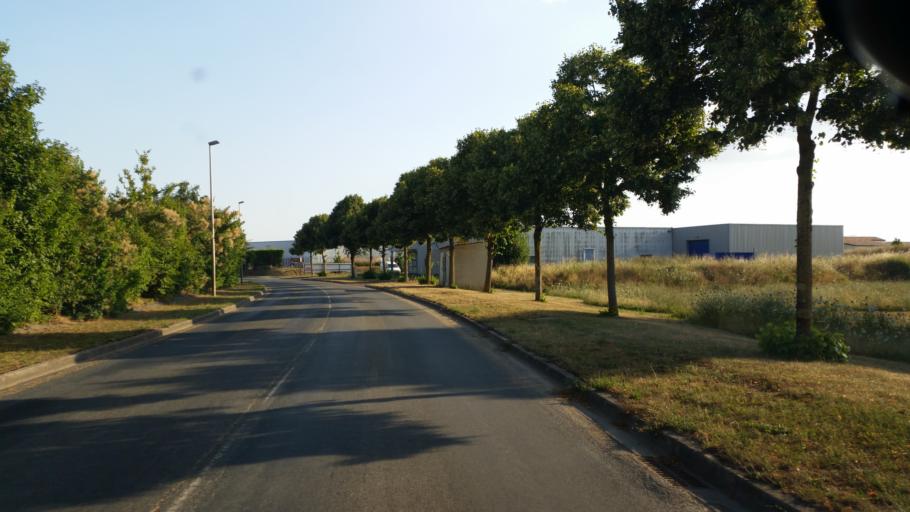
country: FR
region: Poitou-Charentes
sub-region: Departement de la Charente-Maritime
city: Marans
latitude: 46.3088
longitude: -1.0061
